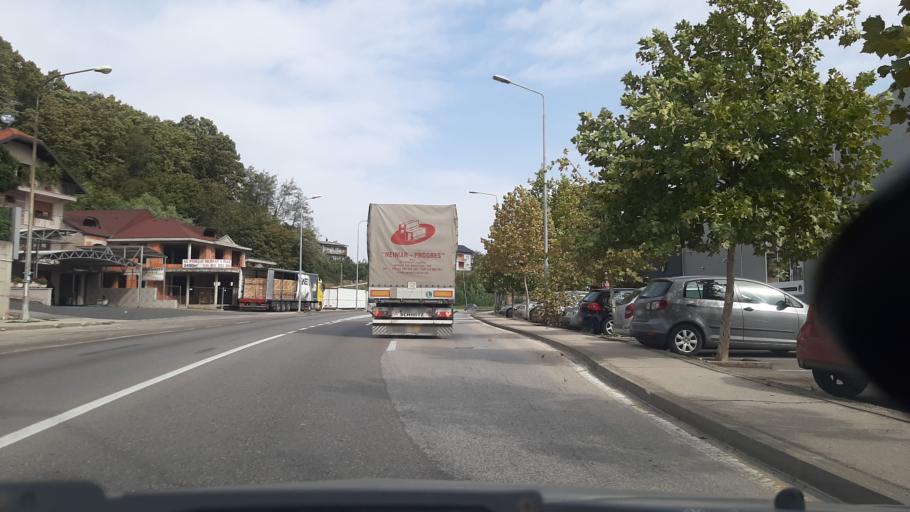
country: BA
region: Republika Srpska
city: Laktasi
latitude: 44.8796
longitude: 17.2840
